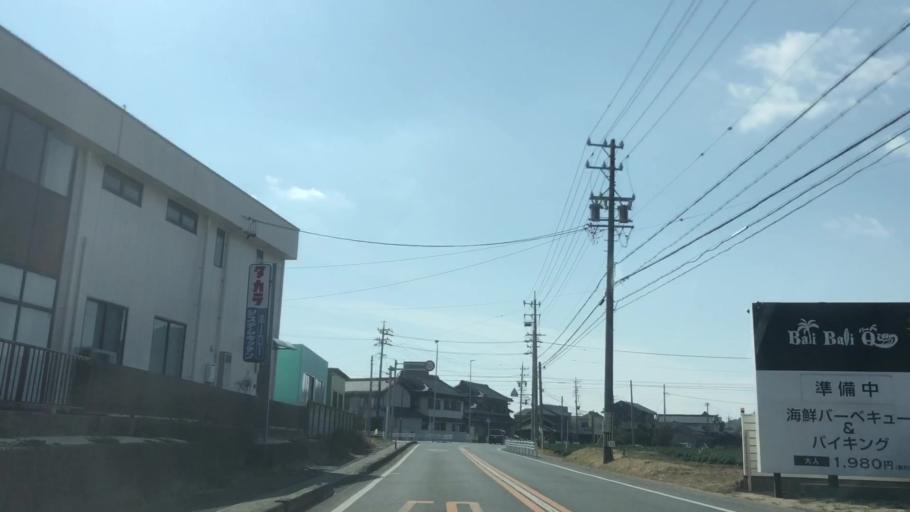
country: JP
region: Aichi
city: Tahara
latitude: 34.6045
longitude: 137.1753
